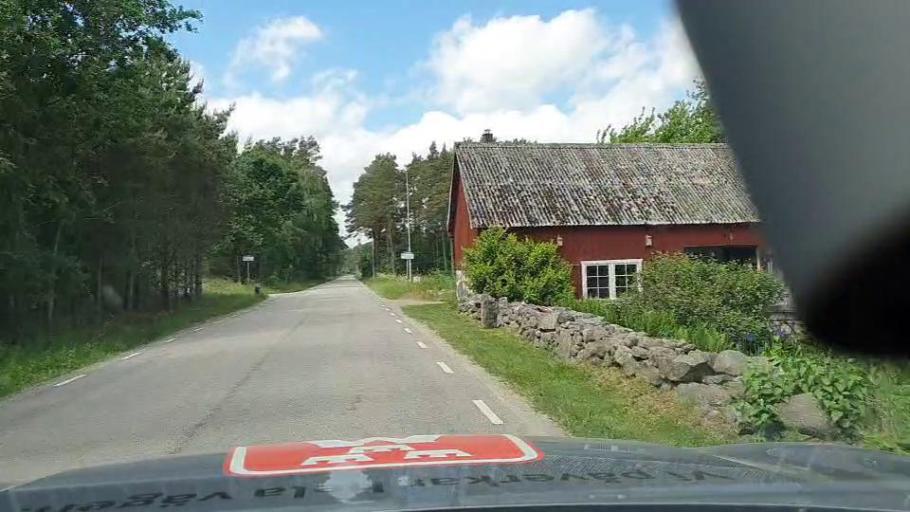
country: SE
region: Blekinge
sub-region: Karlshamns Kommun
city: Morrum
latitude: 56.0928
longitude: 14.6960
